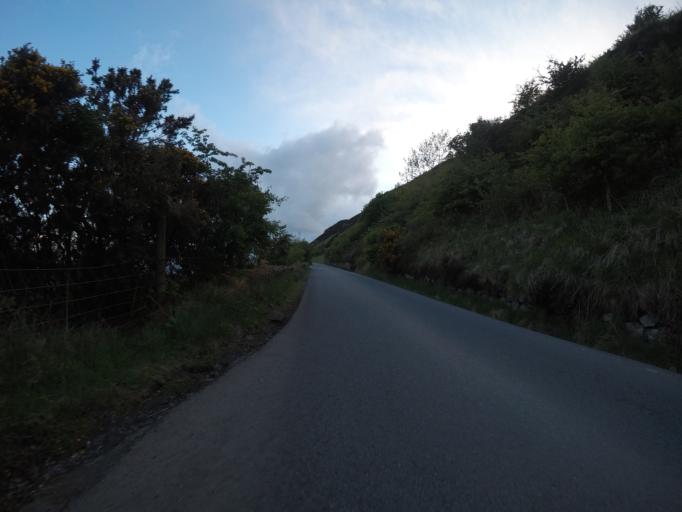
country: GB
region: Scotland
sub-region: Highland
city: Portree
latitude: 57.5916
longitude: -6.3763
